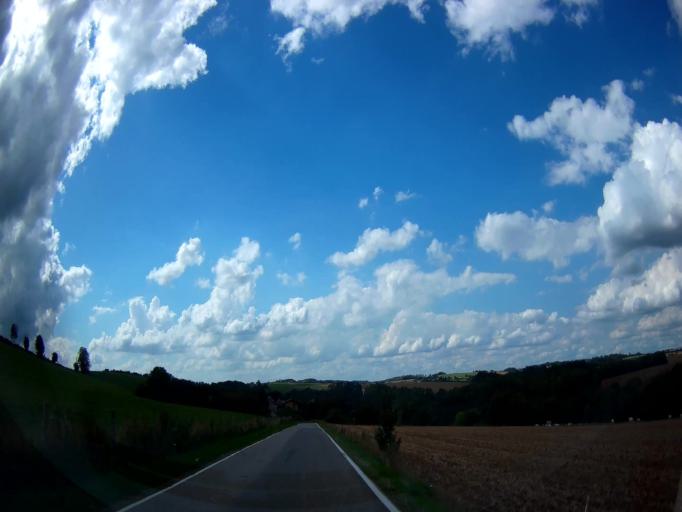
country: BE
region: Wallonia
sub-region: Province de Namur
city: Assesse
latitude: 50.3542
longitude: 4.9741
